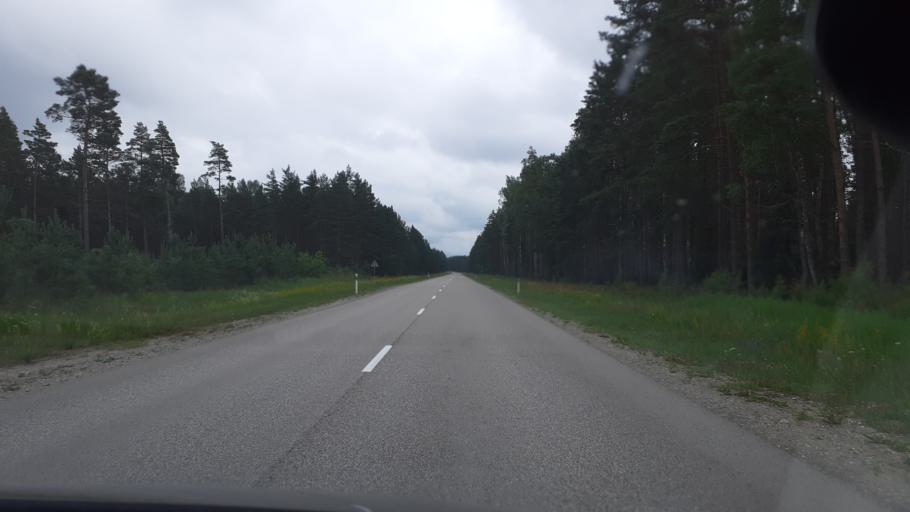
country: LV
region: Ventspils Rajons
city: Piltene
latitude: 57.1257
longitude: 21.7377
